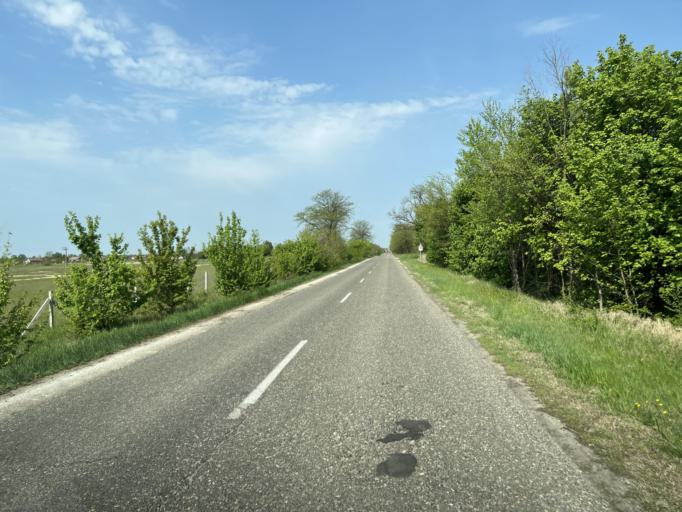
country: HU
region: Pest
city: Tortel
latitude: 47.1168
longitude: 19.9603
